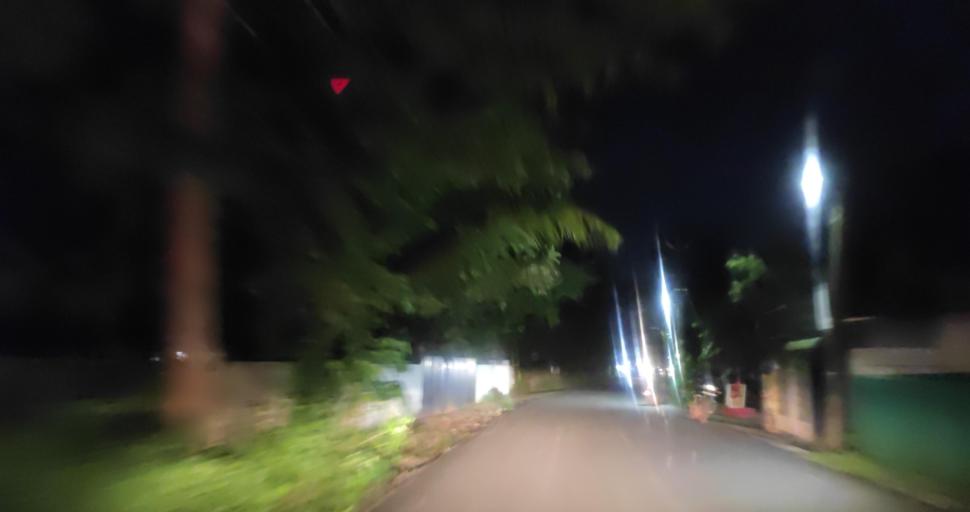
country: IN
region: Kerala
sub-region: Alappuzha
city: Vayalar
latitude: 9.6774
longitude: 76.3034
